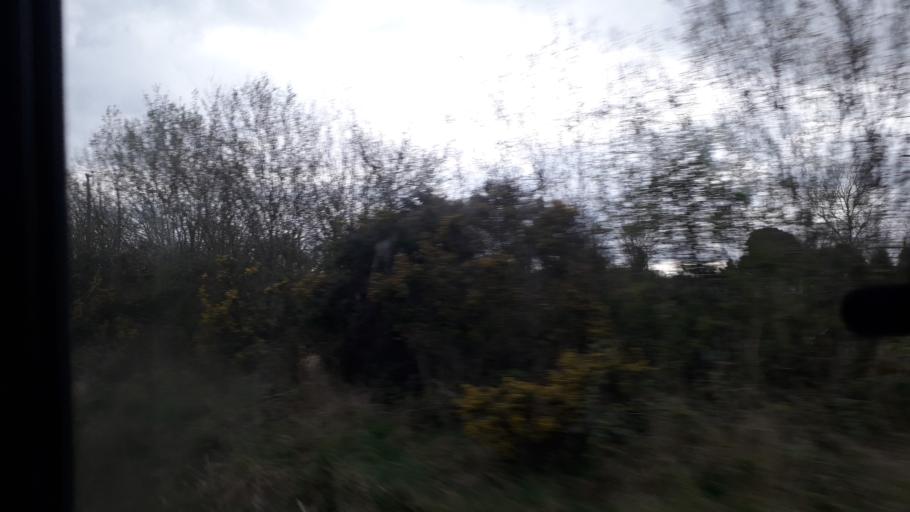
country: IE
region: Leinster
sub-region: An Longfort
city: Longford
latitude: 53.7931
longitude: -7.8466
